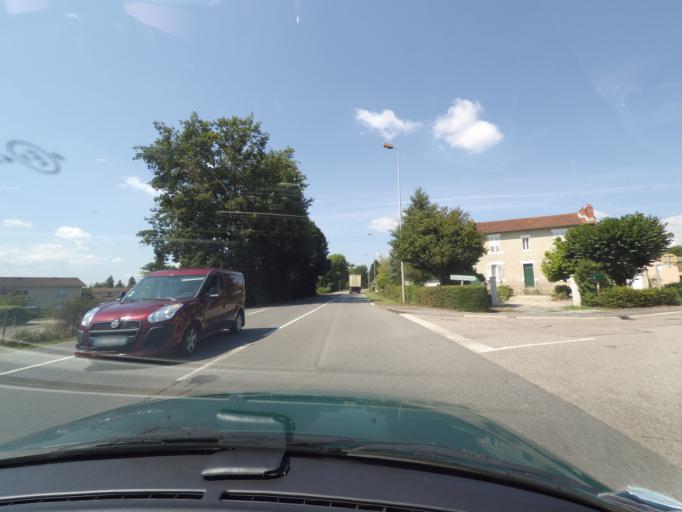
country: FR
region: Limousin
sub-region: Departement de la Haute-Vienne
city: Feytiat
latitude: 45.8127
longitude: 1.3297
